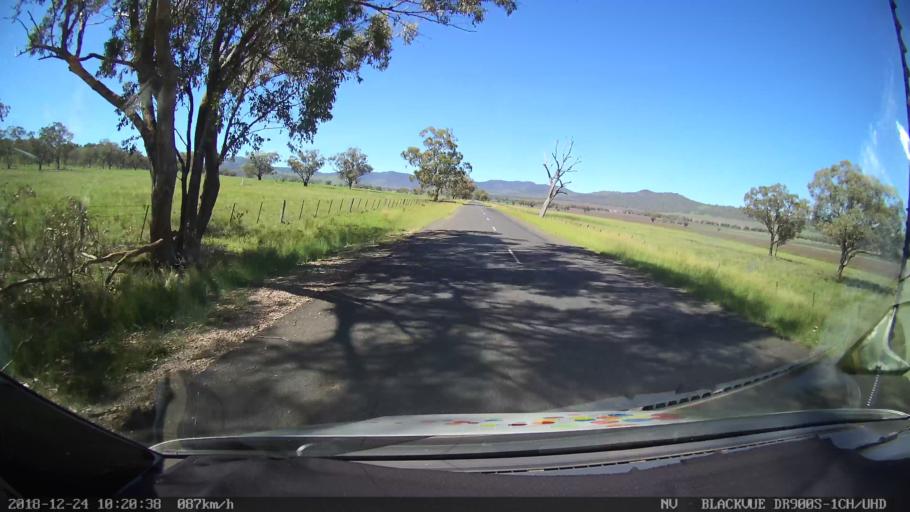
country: AU
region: New South Wales
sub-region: Liverpool Plains
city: Quirindi
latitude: -31.7428
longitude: 150.5561
